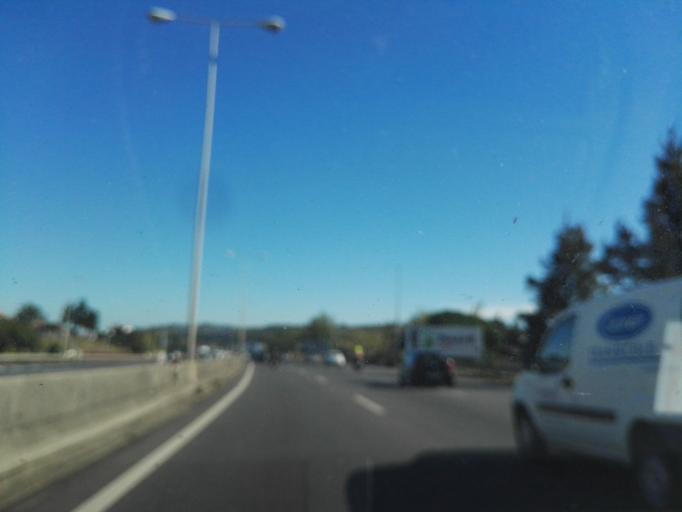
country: PT
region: Lisbon
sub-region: Amadora
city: Amadora
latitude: 38.7400
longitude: -9.2153
